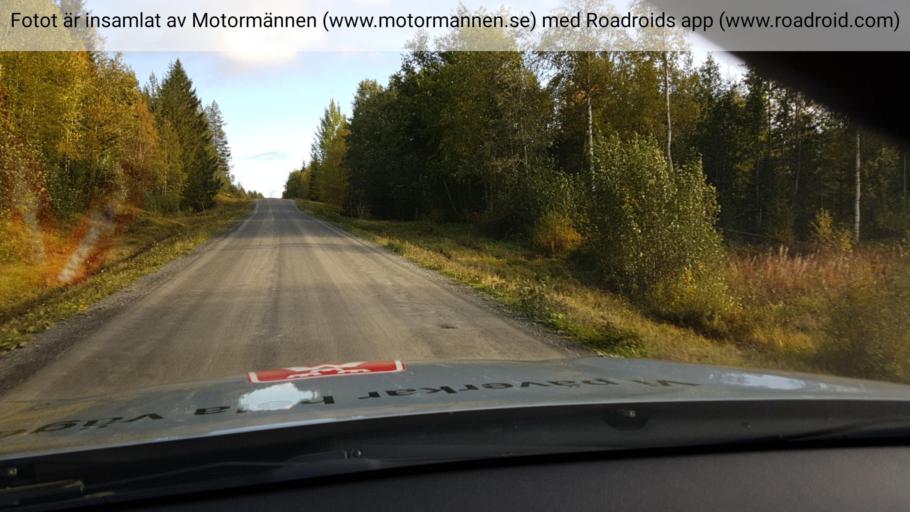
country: SE
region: Jaemtland
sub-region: Krokoms Kommun
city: Krokom
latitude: 63.6890
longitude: 14.5697
